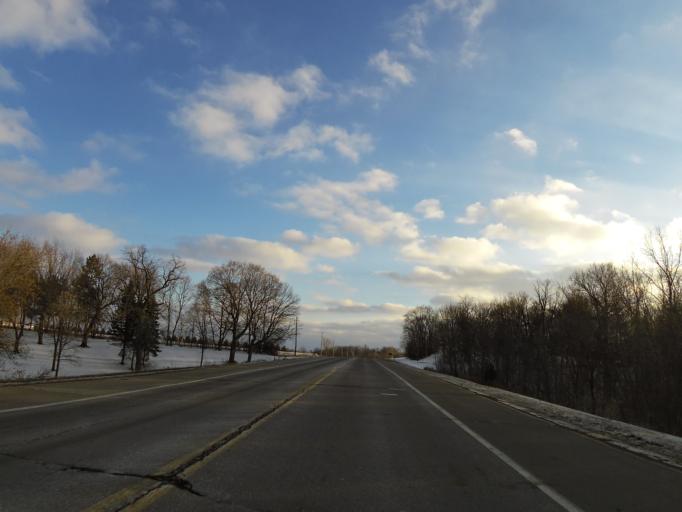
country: US
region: Minnesota
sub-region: Scott County
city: Prior Lake
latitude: 44.7076
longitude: -93.4905
